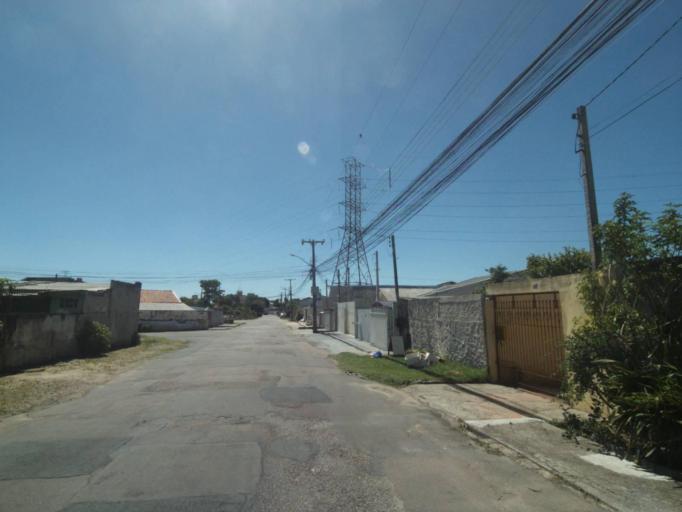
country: BR
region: Parana
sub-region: Curitiba
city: Curitiba
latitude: -25.4770
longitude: -49.3419
